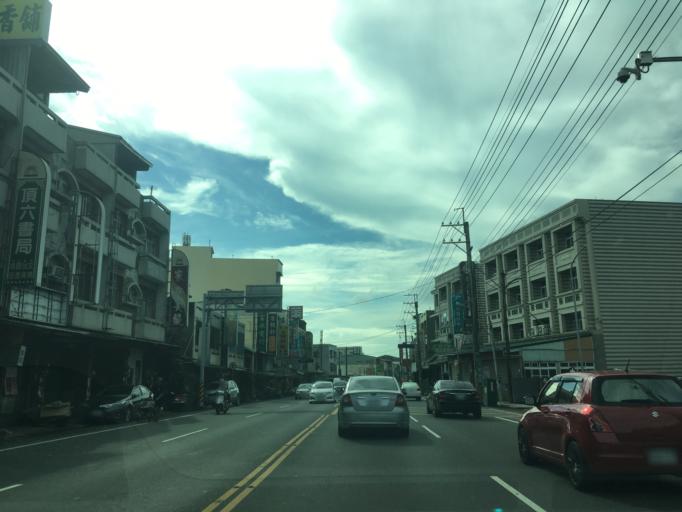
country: TW
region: Taiwan
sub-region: Chiayi
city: Jiayi Shi
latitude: 23.4460
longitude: 120.4944
